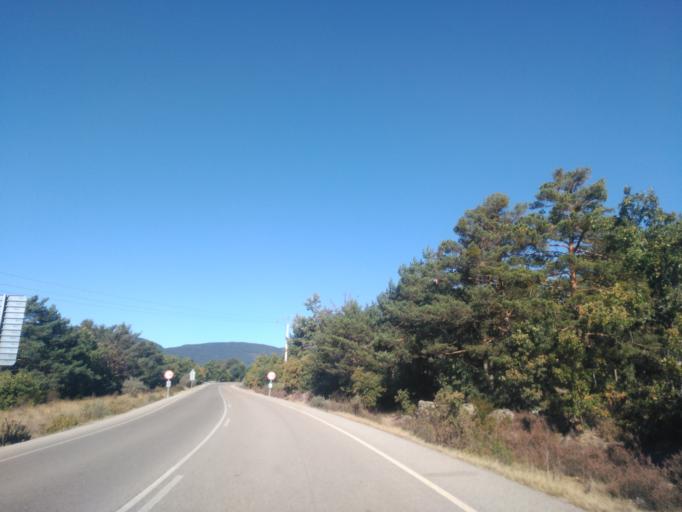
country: ES
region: Castille and Leon
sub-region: Provincia de Soria
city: Vinuesa
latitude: 41.8931
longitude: -2.7302
